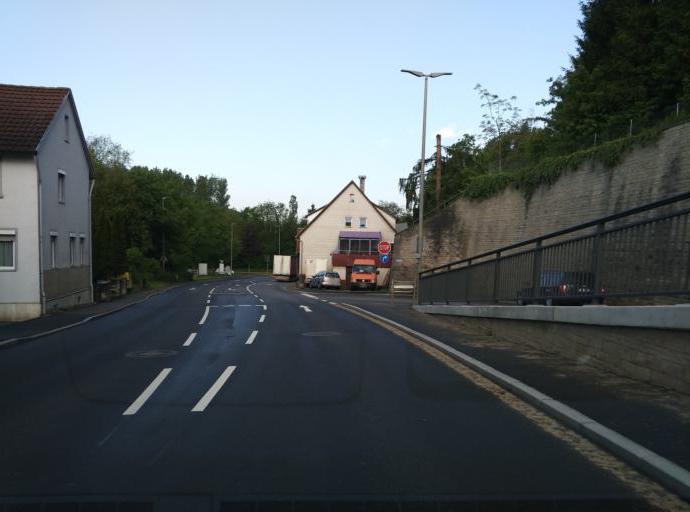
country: DE
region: Baden-Wuerttemberg
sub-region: Tuebingen Region
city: Pliezhausen
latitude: 48.5557
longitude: 9.2043
